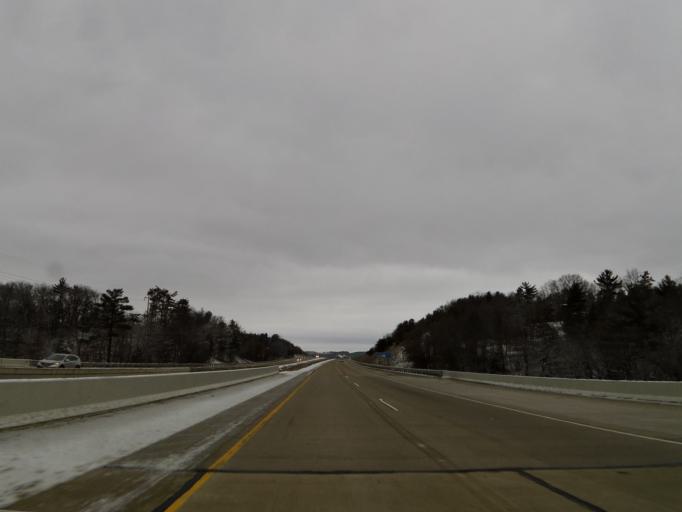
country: US
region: Wisconsin
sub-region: Eau Claire County
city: Eau Claire
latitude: 44.7742
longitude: -91.5209
